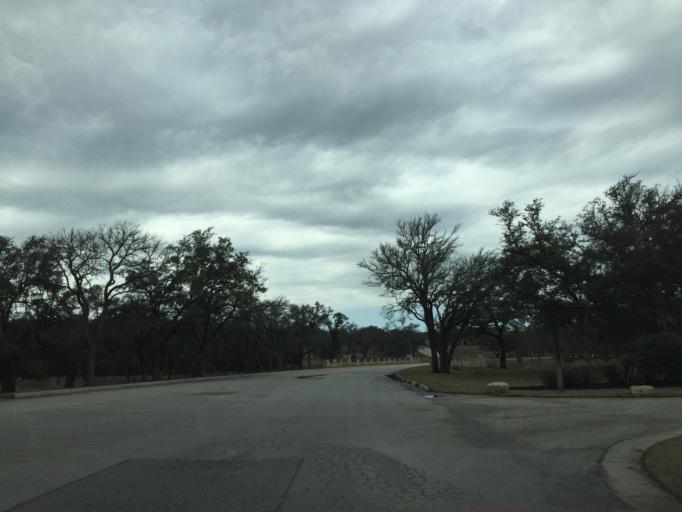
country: US
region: Texas
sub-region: Burnet County
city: Bertram
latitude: 30.7171
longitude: -97.9303
